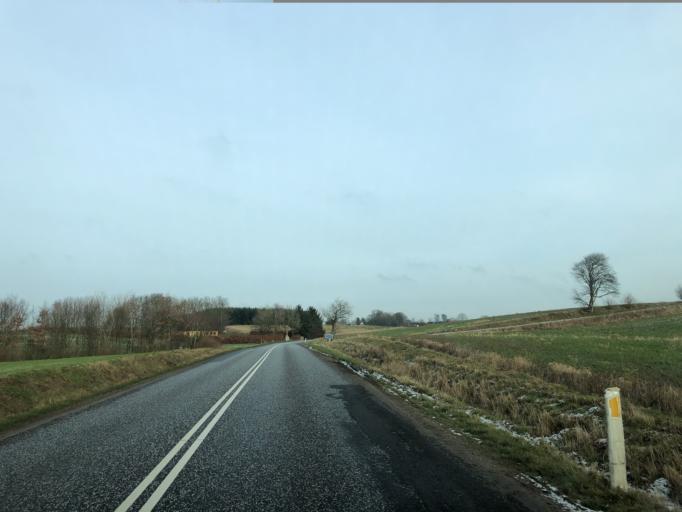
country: DK
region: Central Jutland
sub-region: Hedensted Kommune
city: Torring
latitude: 55.8082
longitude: 9.4633
